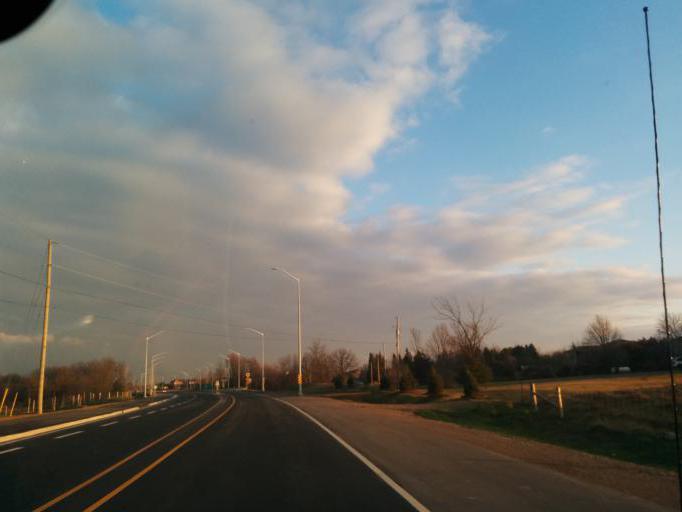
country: CA
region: Ontario
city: Brampton
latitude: 43.8780
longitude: -79.7677
